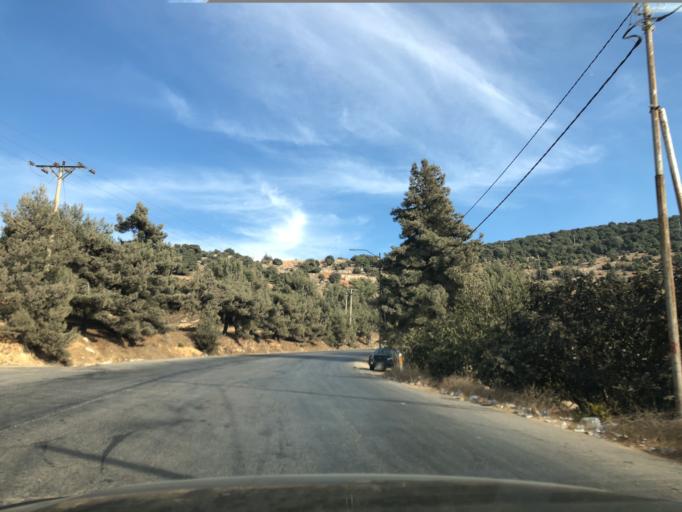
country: JO
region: Irbid
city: `Anjarah
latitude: 32.3125
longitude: 35.7779
